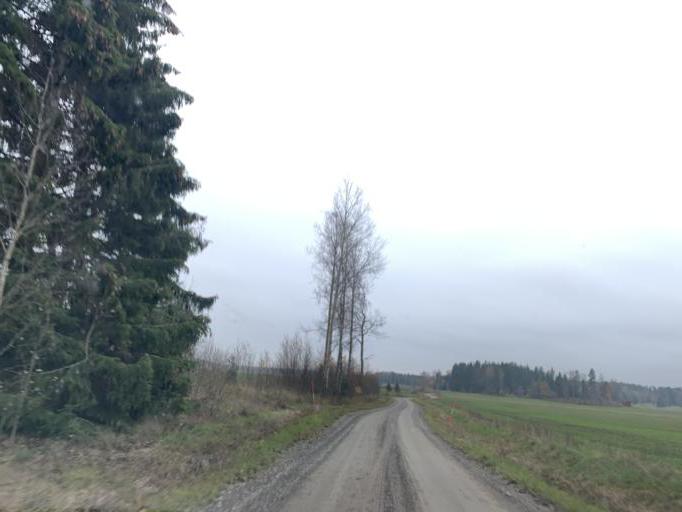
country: SE
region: Vaestmanland
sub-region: Kopings Kommun
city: Koping
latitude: 59.6147
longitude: 16.0753
